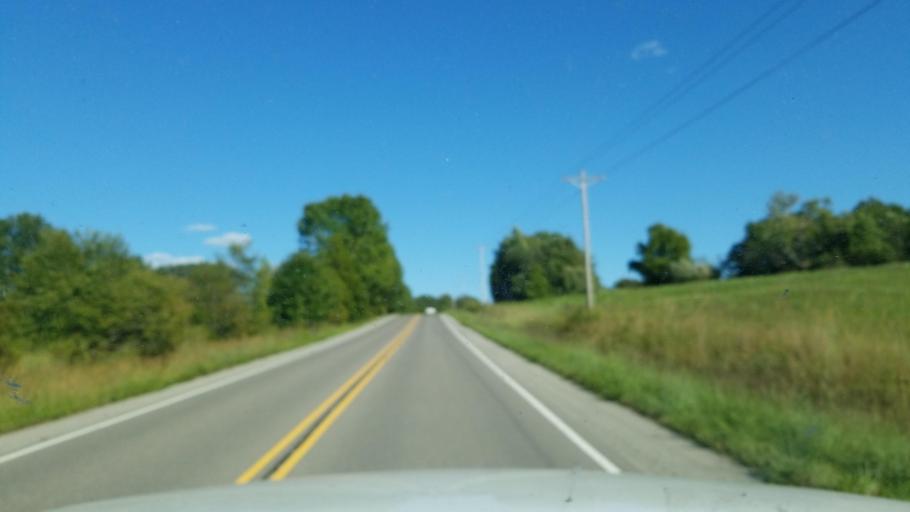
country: US
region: Illinois
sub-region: Hardin County
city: Rosiclare
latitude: 37.5749
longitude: -88.4248
